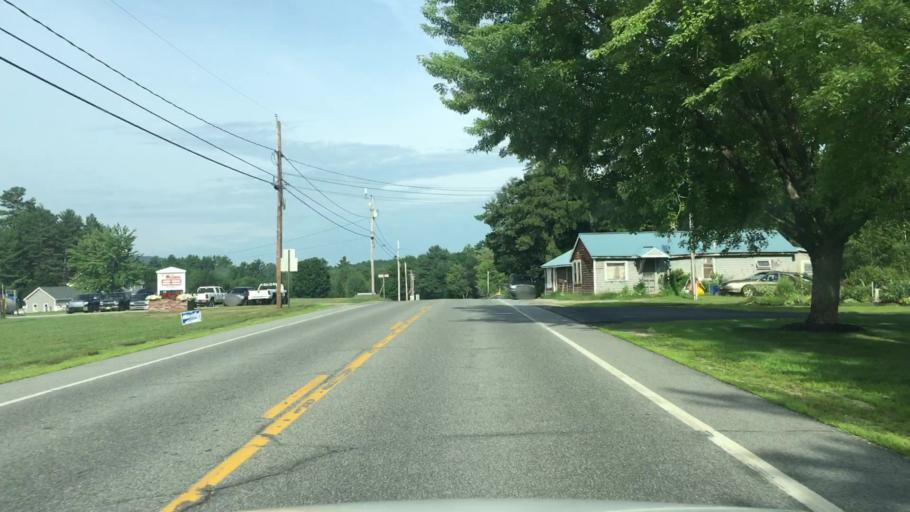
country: US
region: Maine
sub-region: Oxford County
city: Porter
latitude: 43.7954
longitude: -70.9385
